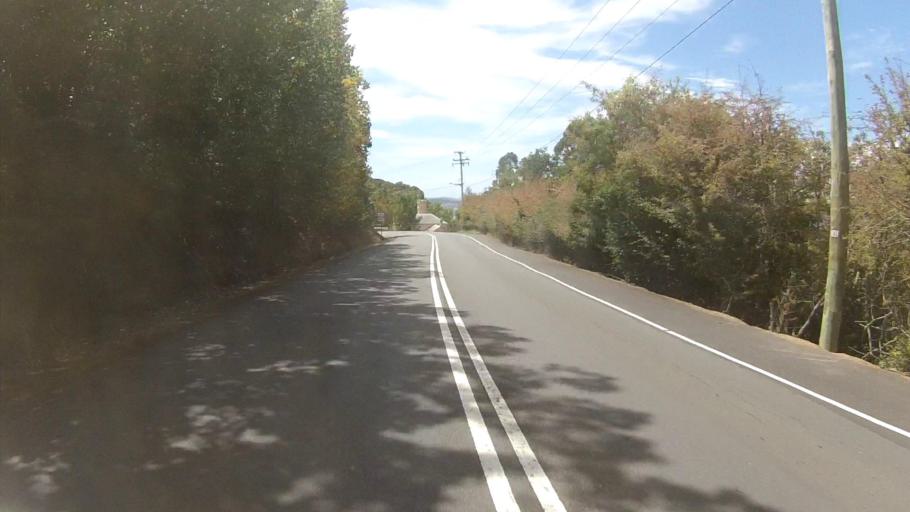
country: AU
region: Tasmania
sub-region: Kingborough
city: Taroona
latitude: -42.9588
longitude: 147.3359
